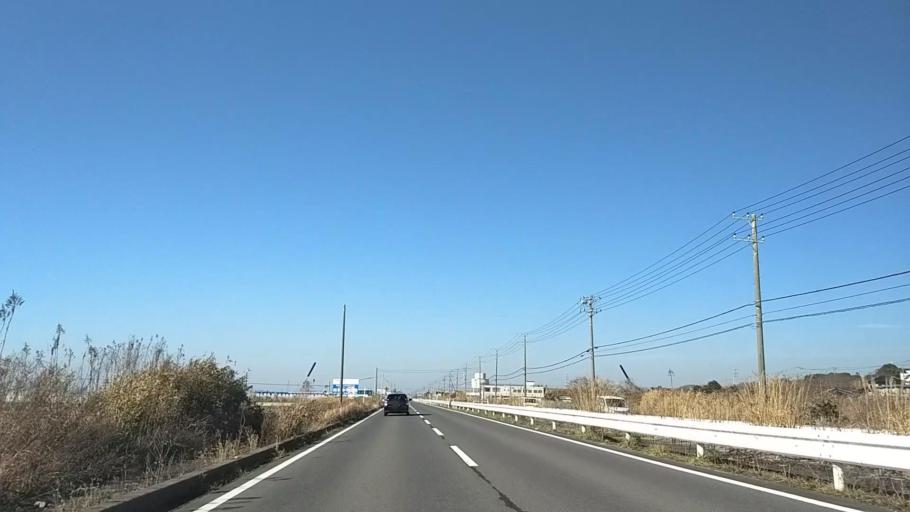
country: JP
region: Chiba
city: Asahi
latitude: 35.7157
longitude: 140.7058
